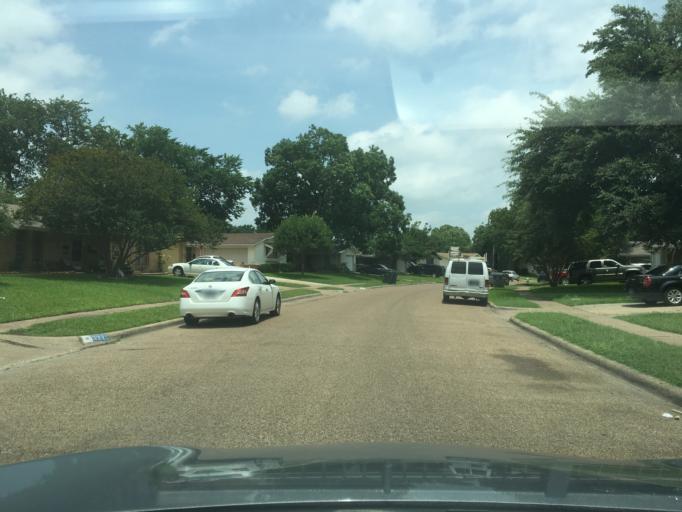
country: US
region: Texas
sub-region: Dallas County
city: Garland
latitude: 32.9188
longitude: -96.6786
